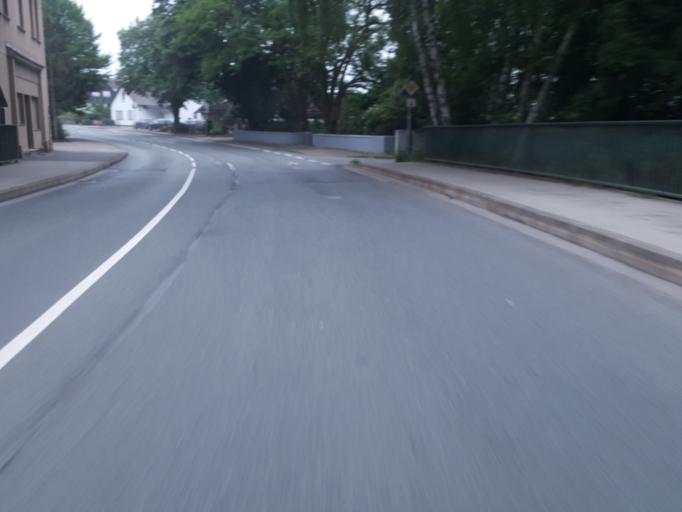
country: DE
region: North Rhine-Westphalia
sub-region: Regierungsbezirk Detmold
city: Kirchlengern
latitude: 52.1954
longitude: 8.6412
